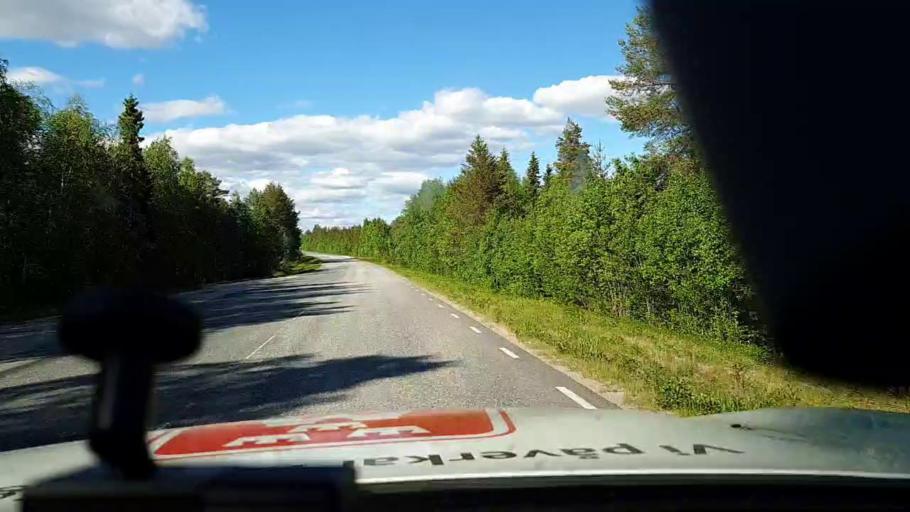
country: FI
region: Lapland
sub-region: Torniolaakso
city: Ylitornio
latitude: 66.3405
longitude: 23.6464
